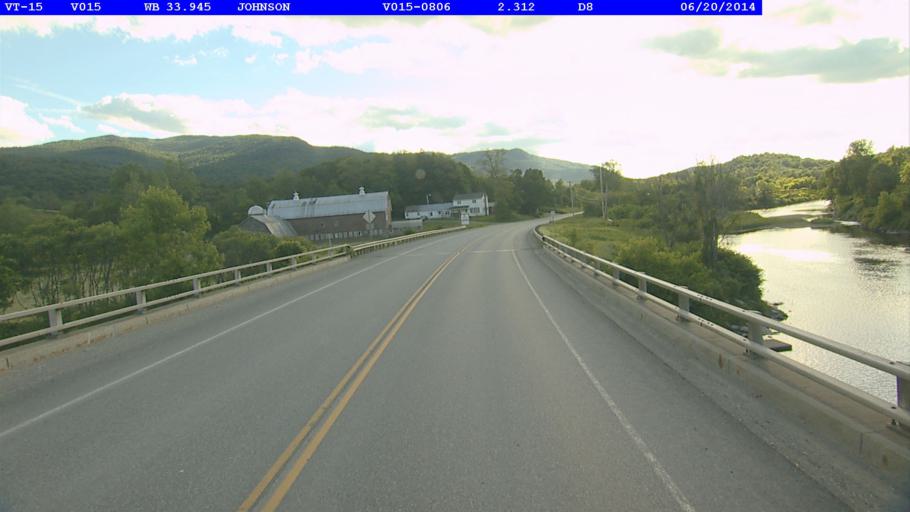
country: US
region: Vermont
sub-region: Lamoille County
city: Johnson
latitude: 44.6427
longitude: -72.7106
